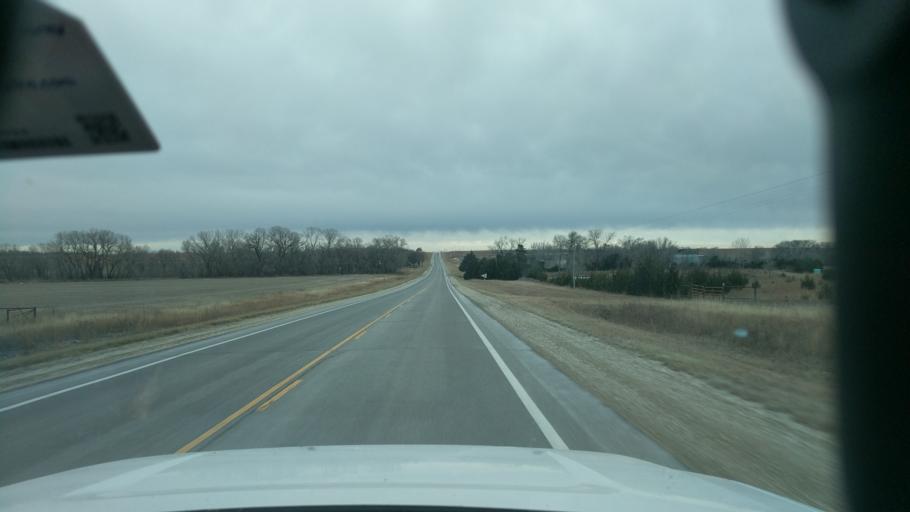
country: US
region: Kansas
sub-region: Marion County
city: Marion
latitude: 38.3853
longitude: -96.9667
